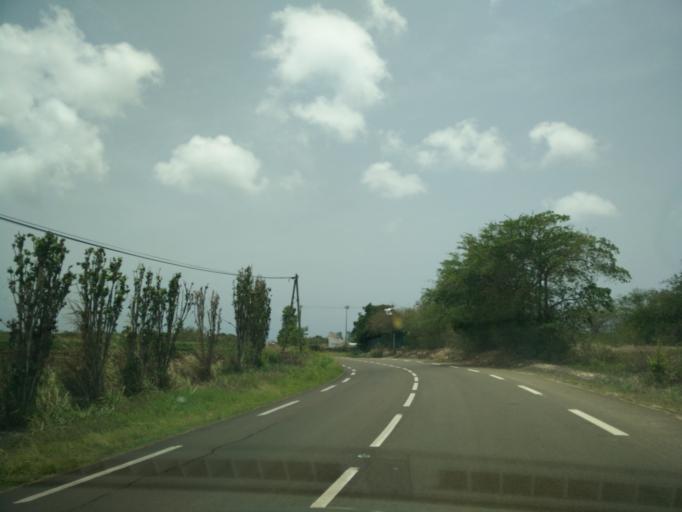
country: GP
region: Guadeloupe
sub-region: Guadeloupe
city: Anse-Bertrand
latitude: 16.4629
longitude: -61.5106
